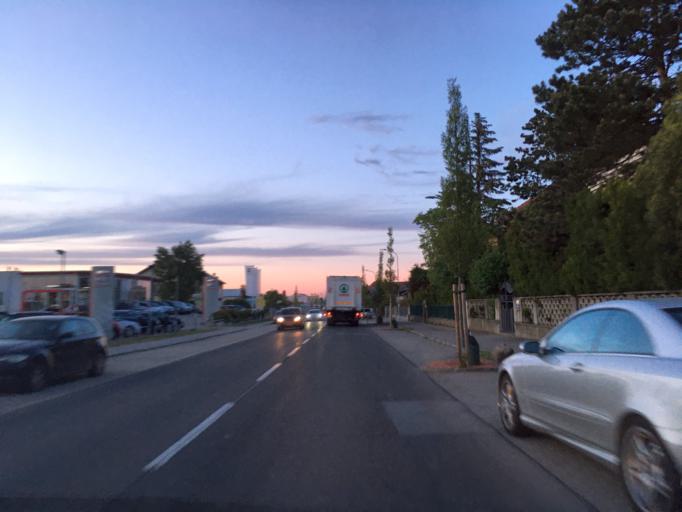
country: AT
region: Lower Austria
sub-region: Politischer Bezirk Wien-Umgebung
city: Zwolfaxing
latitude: 48.1174
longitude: 16.4676
